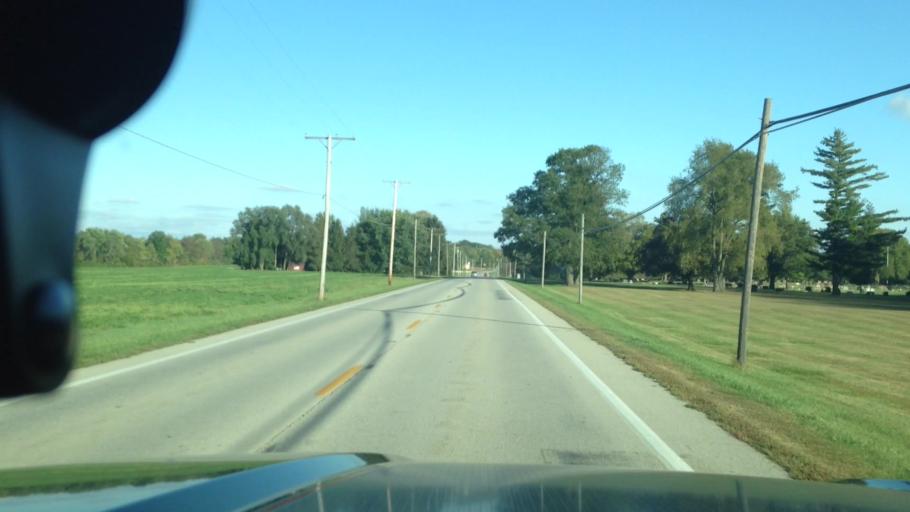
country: US
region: Ohio
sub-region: Darke County
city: Greenville
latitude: 40.1115
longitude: -84.6552
